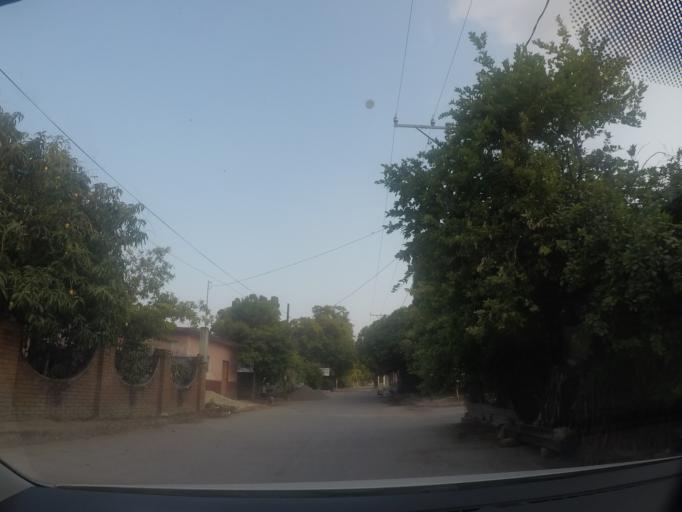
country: MX
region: Oaxaca
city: San Jeronimo Ixtepec
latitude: 16.5852
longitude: -95.2100
